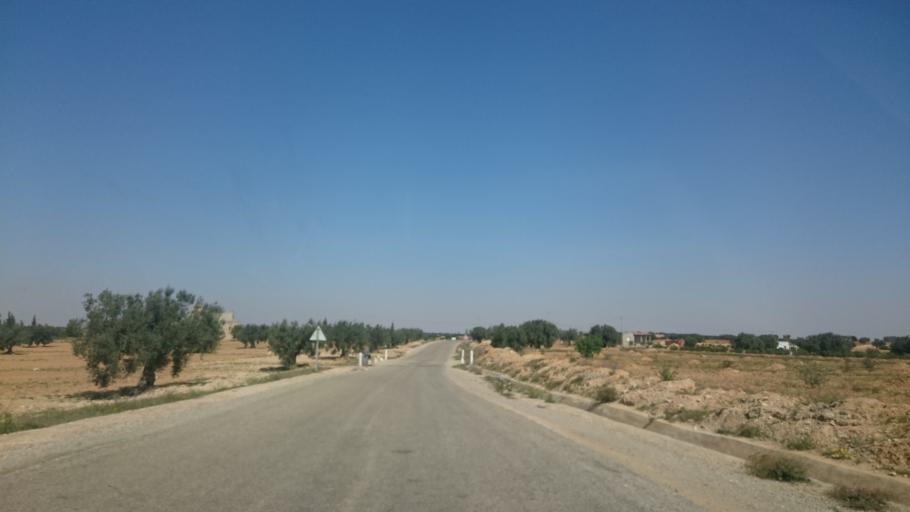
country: TN
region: Safaqis
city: Sfax
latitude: 34.7803
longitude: 10.5170
